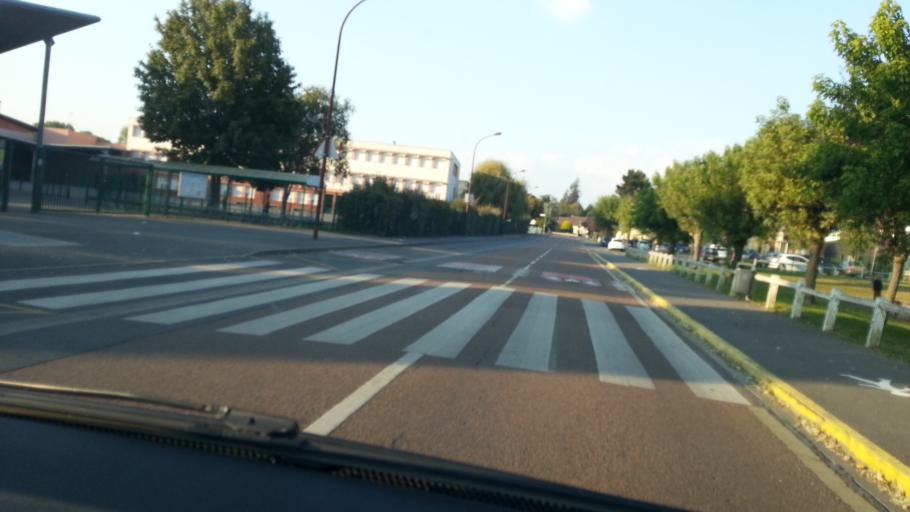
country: FR
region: Picardie
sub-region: Departement de l'Oise
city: Estrees-Saint-Denis
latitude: 49.4282
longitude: 2.6427
